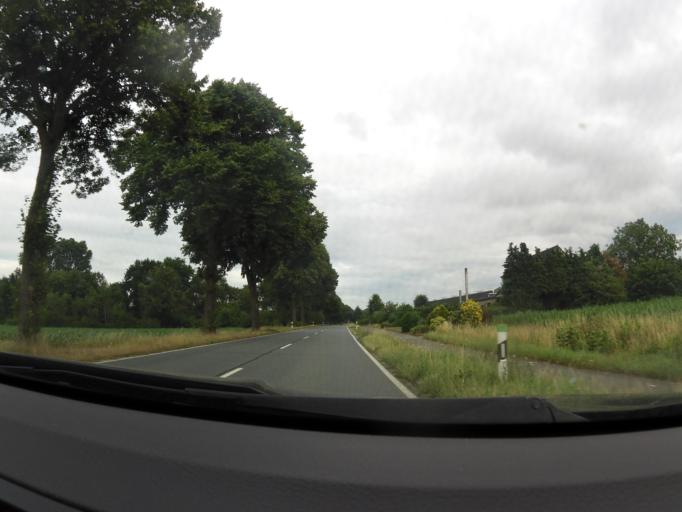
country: DE
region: North Rhine-Westphalia
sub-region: Regierungsbezirk Dusseldorf
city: Kevelaer
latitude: 51.5300
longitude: 6.2607
